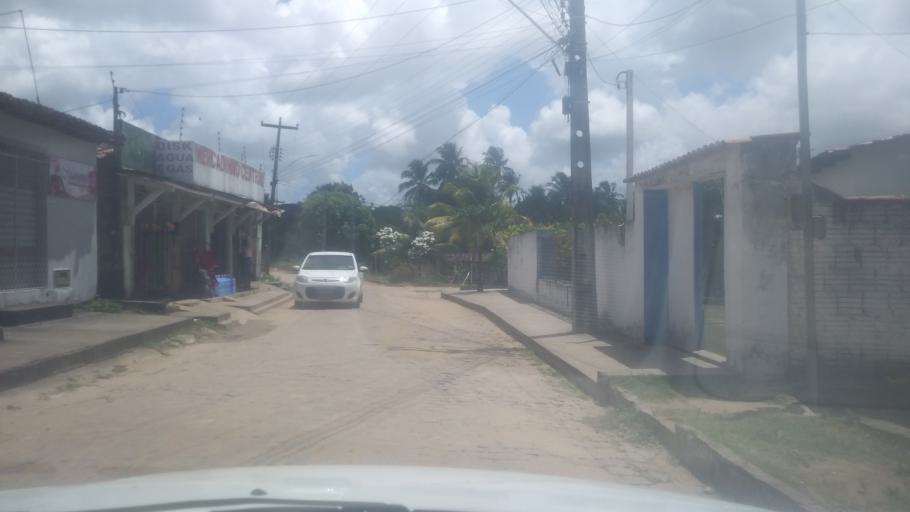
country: BR
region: Rio Grande do Norte
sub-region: Sao Jose De Mipibu
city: Sao Jose de Mipibu
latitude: -6.0721
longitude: -35.2295
